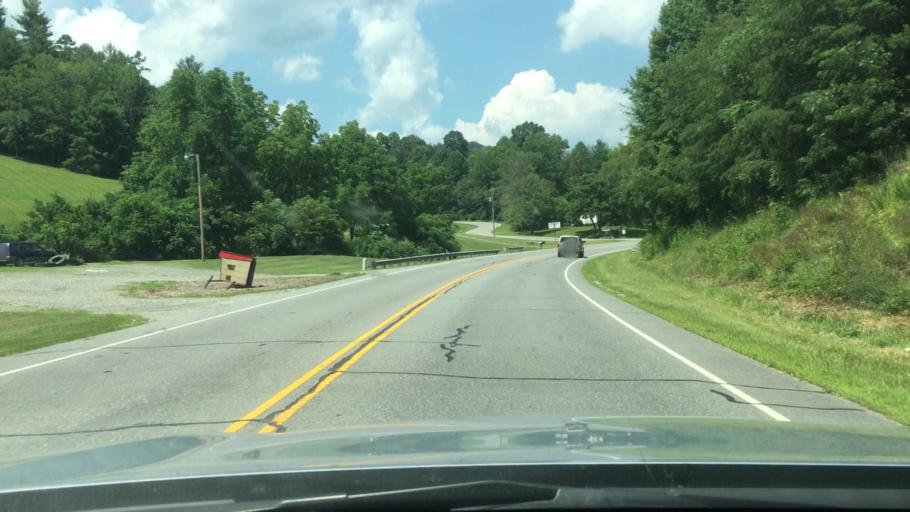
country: US
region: North Carolina
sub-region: Madison County
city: Marshall
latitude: 35.8140
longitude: -82.6549
